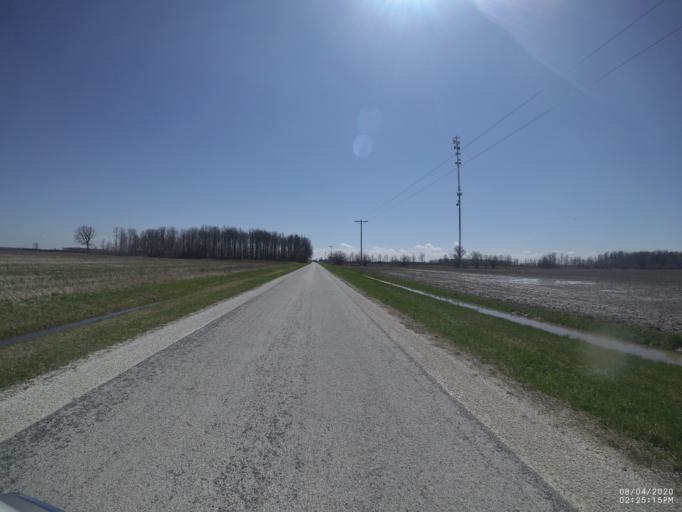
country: US
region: Ohio
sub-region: Sandusky County
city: Gibsonburg
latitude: 41.2999
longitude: -83.2595
